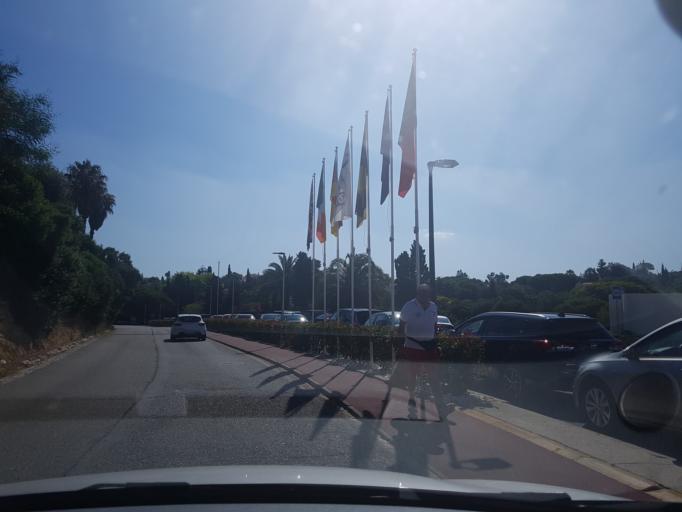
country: PT
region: Faro
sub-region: Lagoa
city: Carvoeiro
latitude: 37.0943
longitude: -8.4596
